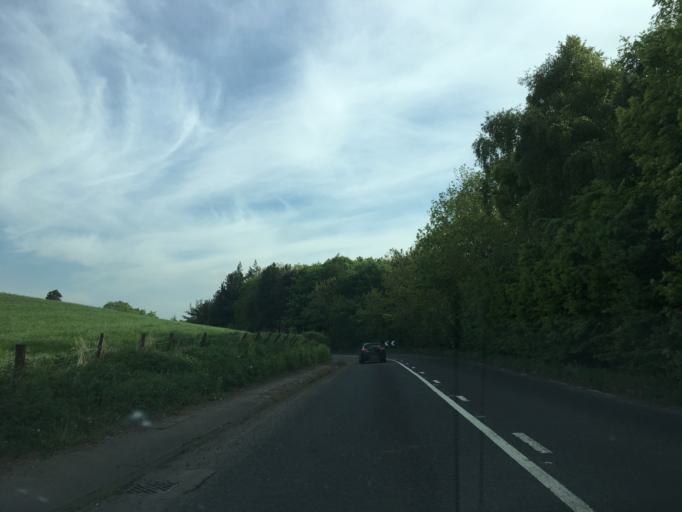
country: GB
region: Scotland
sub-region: Midlothian
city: Loanhead
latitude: 55.8733
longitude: -3.1931
